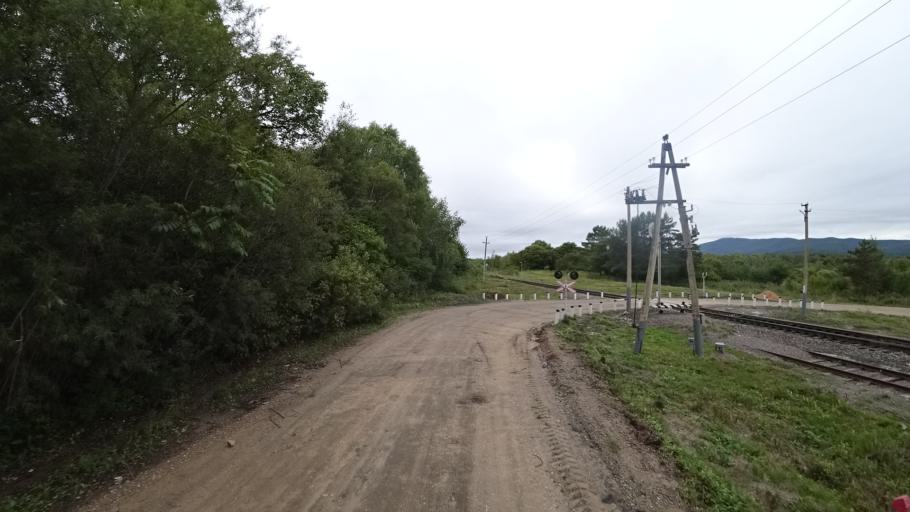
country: RU
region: Primorskiy
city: Rettikhovka
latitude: 44.1628
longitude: 132.7405
